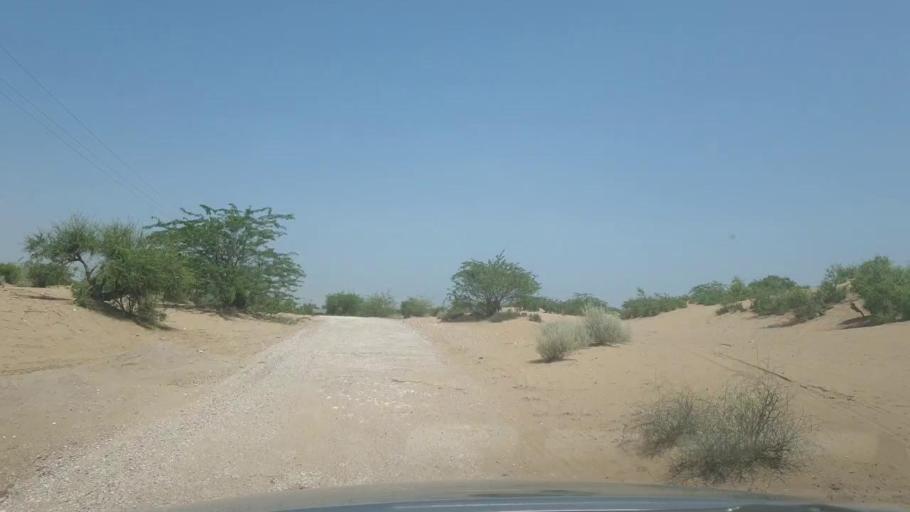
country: PK
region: Sindh
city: Kot Diji
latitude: 27.3274
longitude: 69.0120
